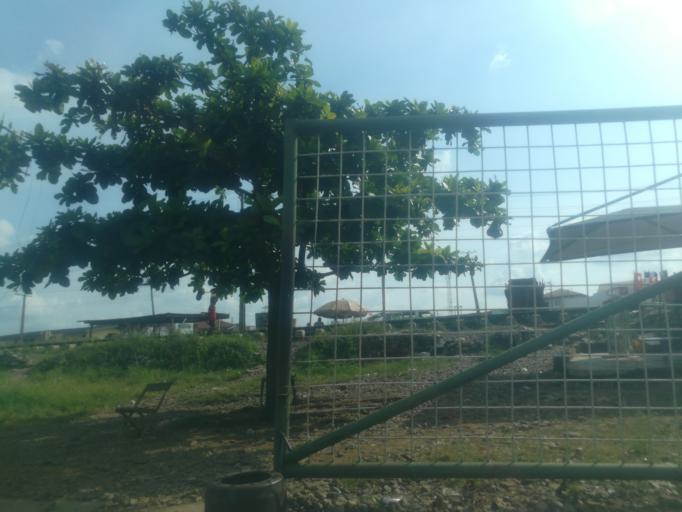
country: NG
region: Oyo
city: Ibadan
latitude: 7.3904
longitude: 3.8188
